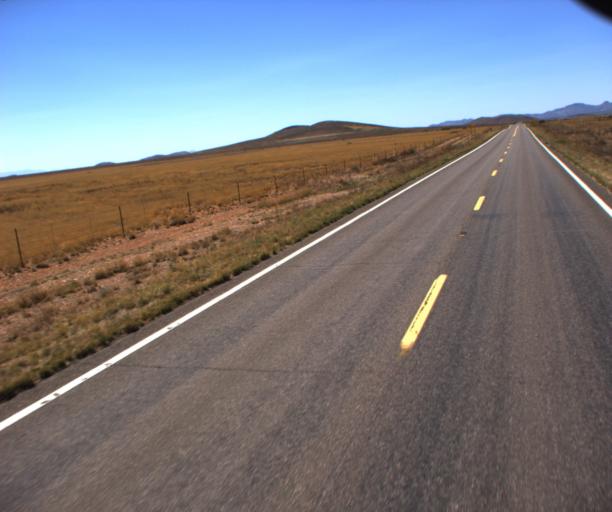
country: US
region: Arizona
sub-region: Cochise County
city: Douglas
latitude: 31.6024
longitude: -109.2301
